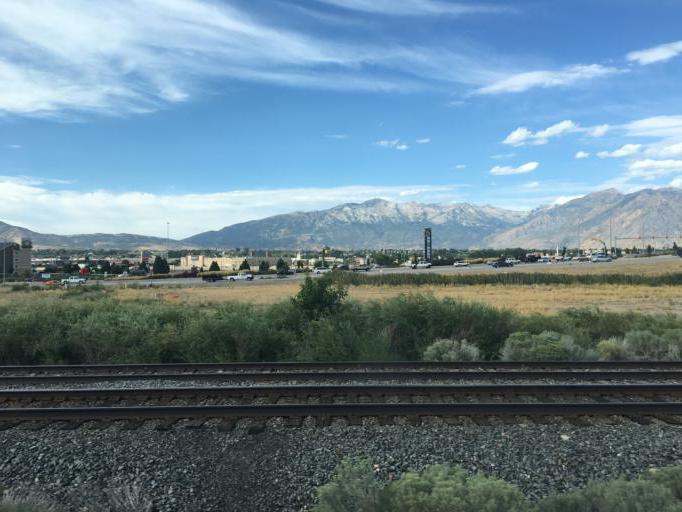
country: US
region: Utah
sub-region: Utah County
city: American Fork
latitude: 40.3752
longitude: -111.8223
